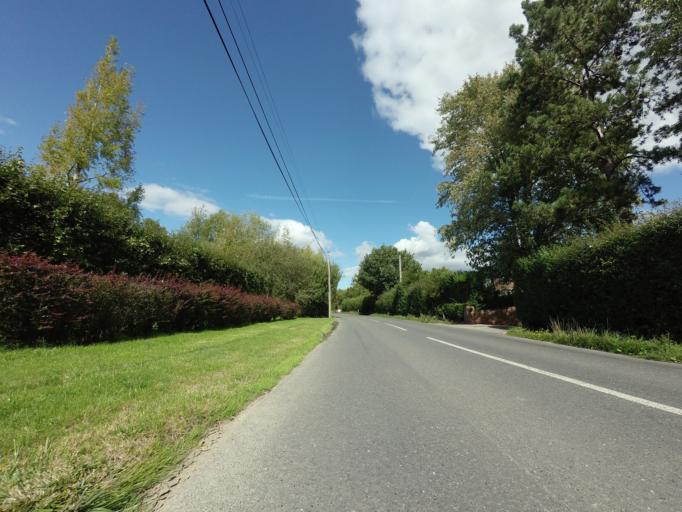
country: GB
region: England
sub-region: Kent
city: Marden
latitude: 51.1565
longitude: 0.4856
